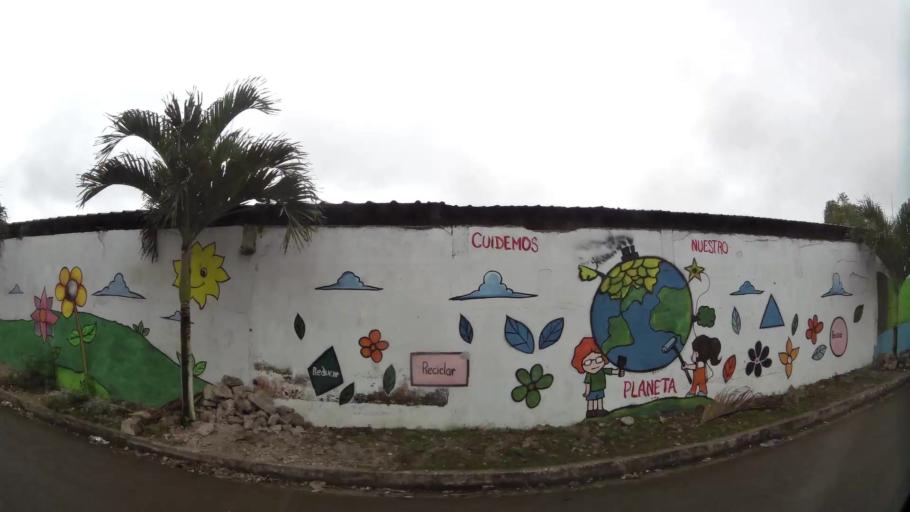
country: EC
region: El Oro
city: Pasaje
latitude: -3.3229
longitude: -79.8092
